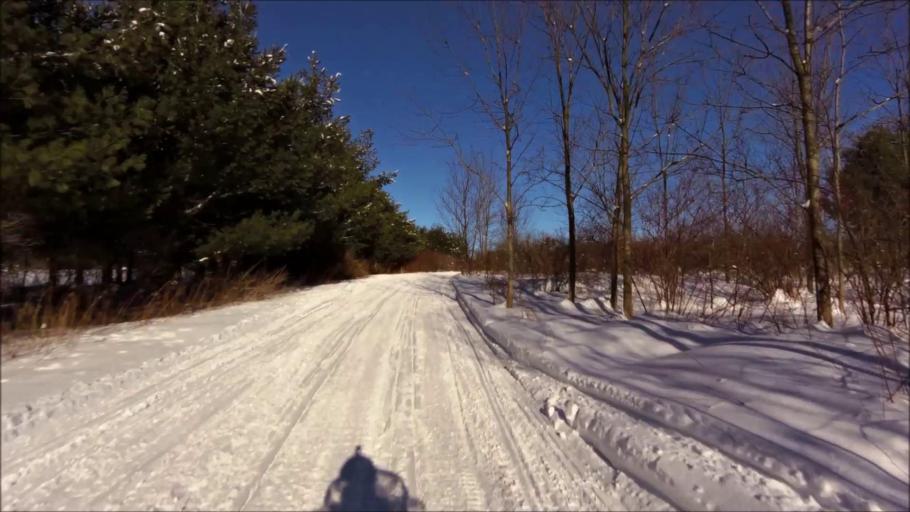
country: US
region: New York
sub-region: Chautauqua County
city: Mayville
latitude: 42.2847
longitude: -79.4321
